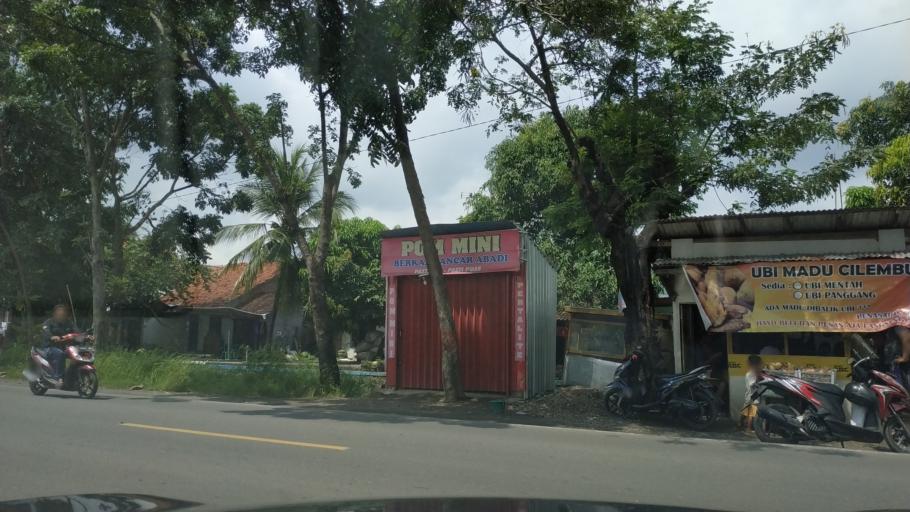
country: ID
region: Central Java
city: Lebaksiu
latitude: -7.0455
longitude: 109.1323
